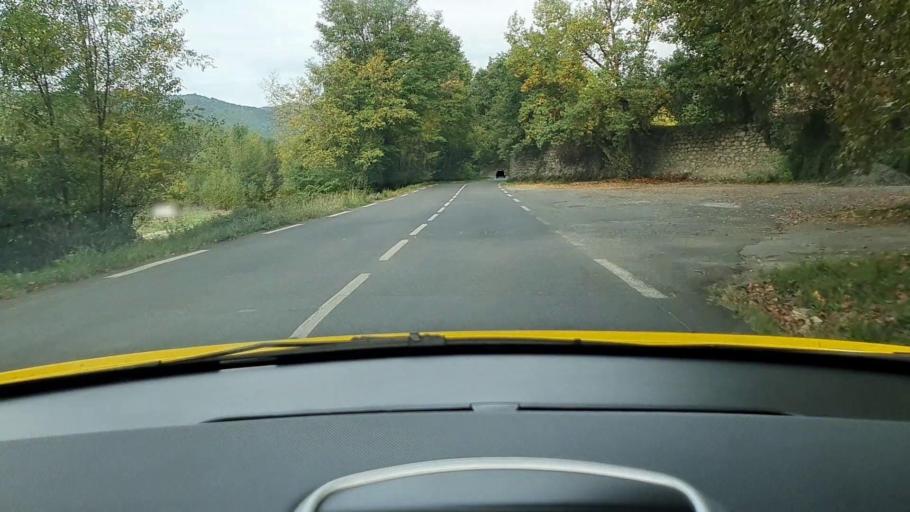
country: FR
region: Languedoc-Roussillon
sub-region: Departement du Gard
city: Le Vigan
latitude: 43.9777
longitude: 3.5890
